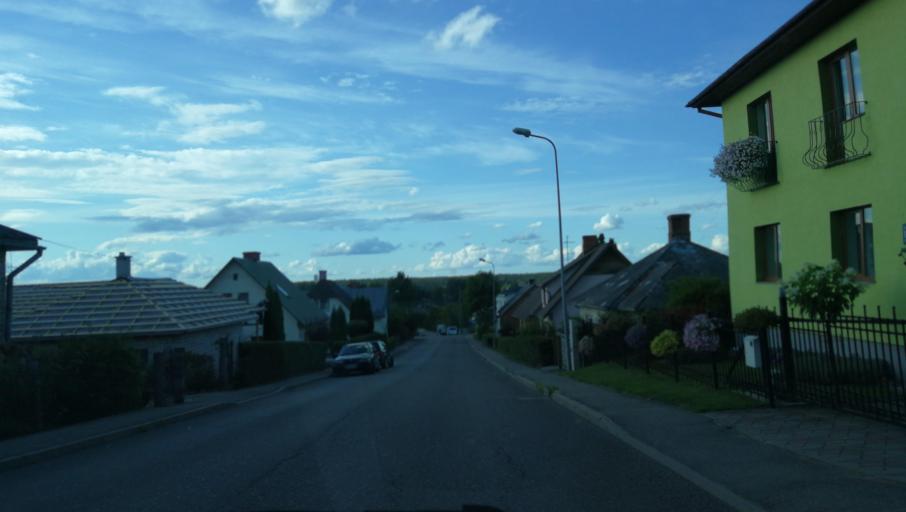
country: LV
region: Cesu Rajons
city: Cesis
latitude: 57.3176
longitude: 25.2768
